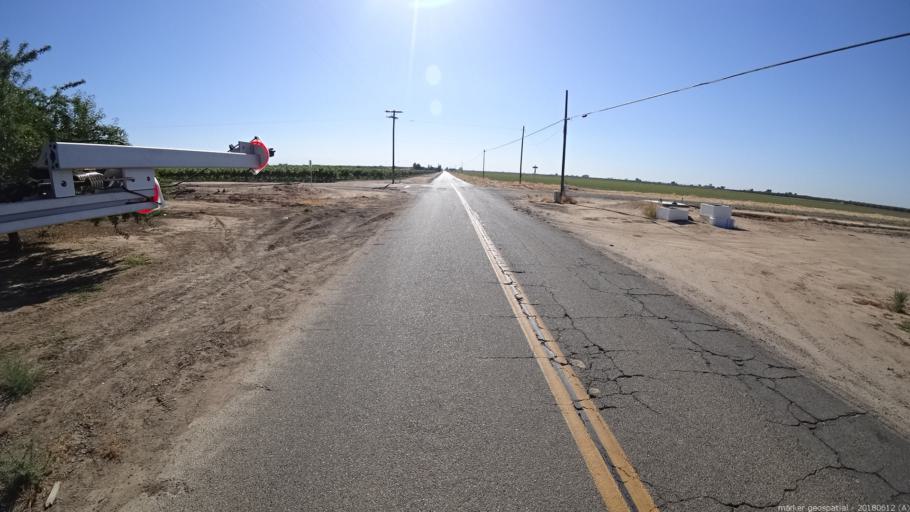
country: US
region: California
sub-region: Madera County
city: Fairmead
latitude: 37.0110
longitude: -120.1665
